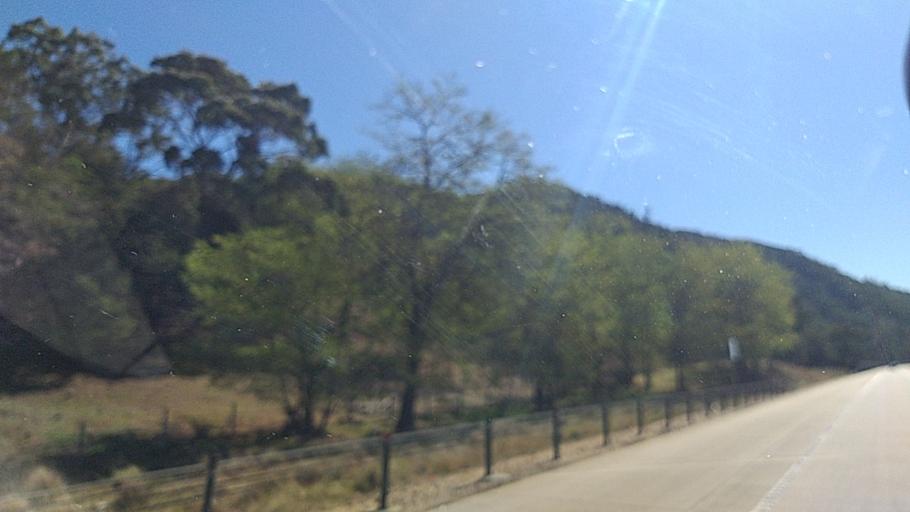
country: AU
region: New South Wales
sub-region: Yass Valley
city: Gundaroo
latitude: -35.0681
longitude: 149.3734
